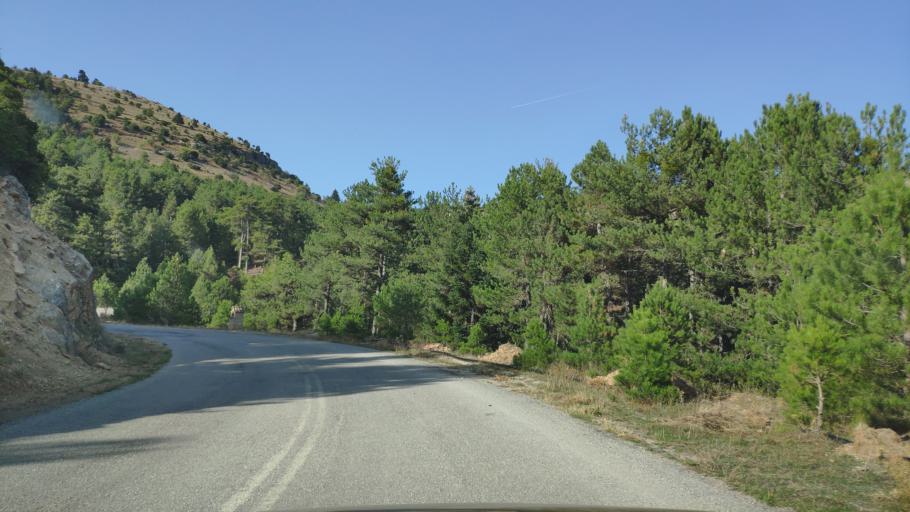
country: GR
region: West Greece
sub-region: Nomos Achaias
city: Aiyira
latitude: 38.0253
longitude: 22.4022
